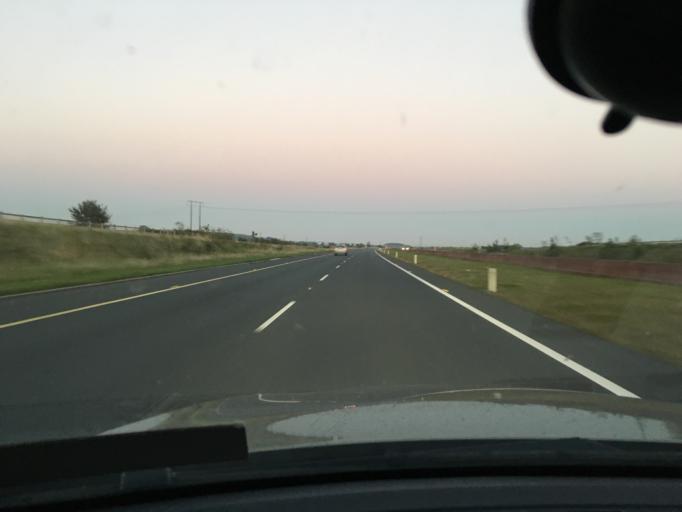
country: IE
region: Connaught
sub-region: County Galway
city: Oranmore
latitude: 53.3002
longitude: -8.8670
